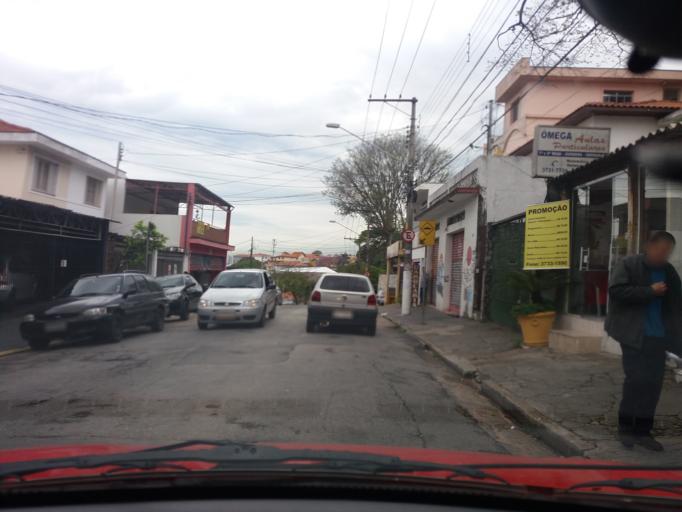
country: BR
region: Sao Paulo
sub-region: Osasco
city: Osasco
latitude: -23.5781
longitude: -46.7416
